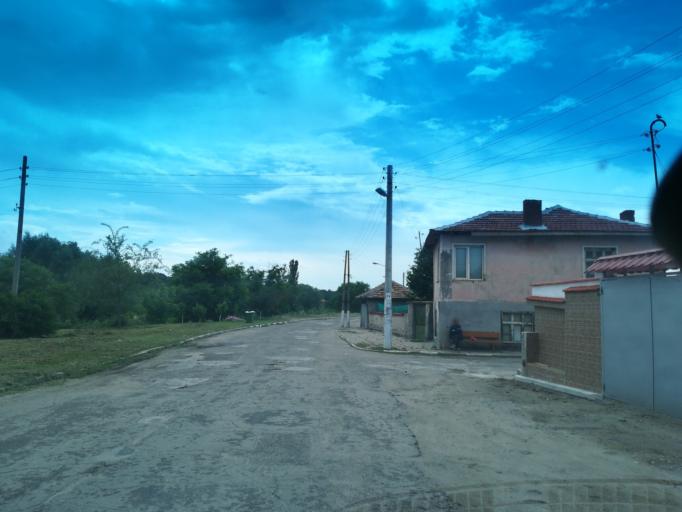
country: BG
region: Khaskovo
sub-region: Obshtina Mineralni Bani
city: Mineralni Bani
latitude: 41.9945
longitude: 25.2291
